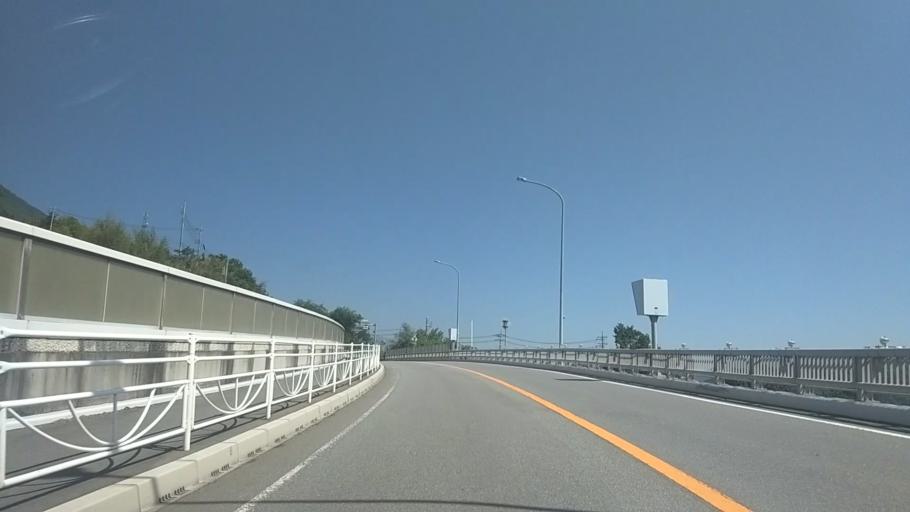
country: JP
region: Shizuoka
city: Fujinomiya
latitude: 35.3817
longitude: 138.4489
